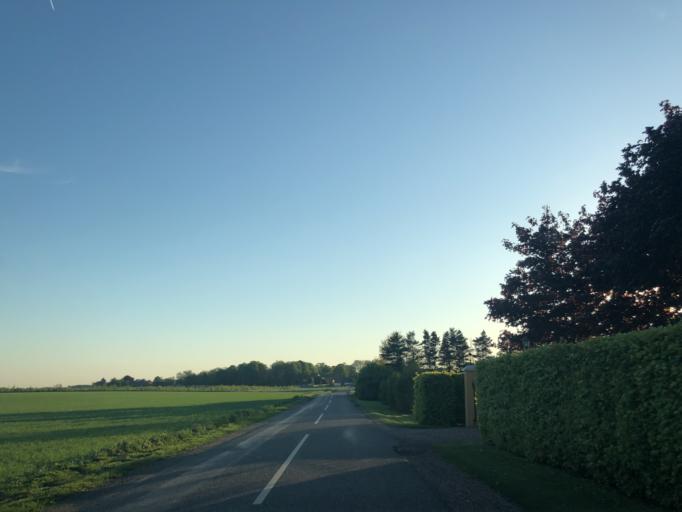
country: DK
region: Zealand
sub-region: Faxe Kommune
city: Haslev
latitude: 55.4107
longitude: 11.8998
